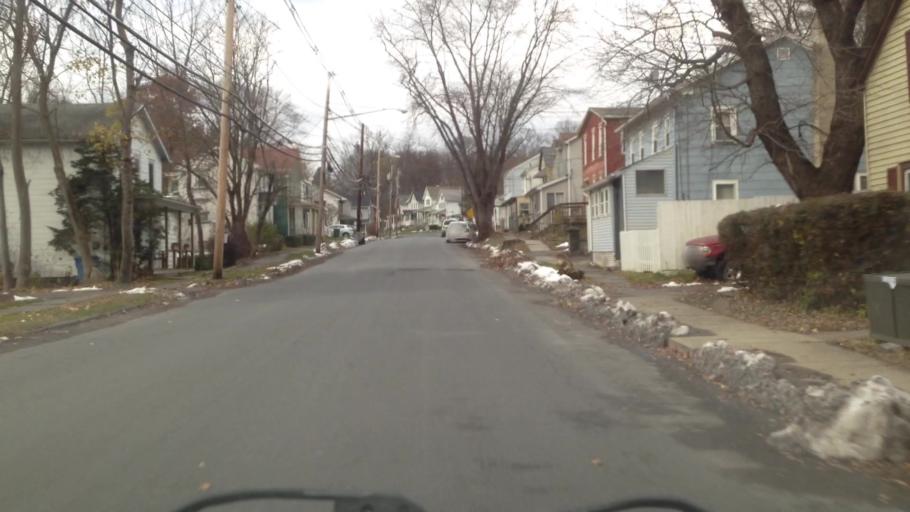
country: US
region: New York
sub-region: Ulster County
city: Saugerties
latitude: 42.0724
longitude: -73.9517
